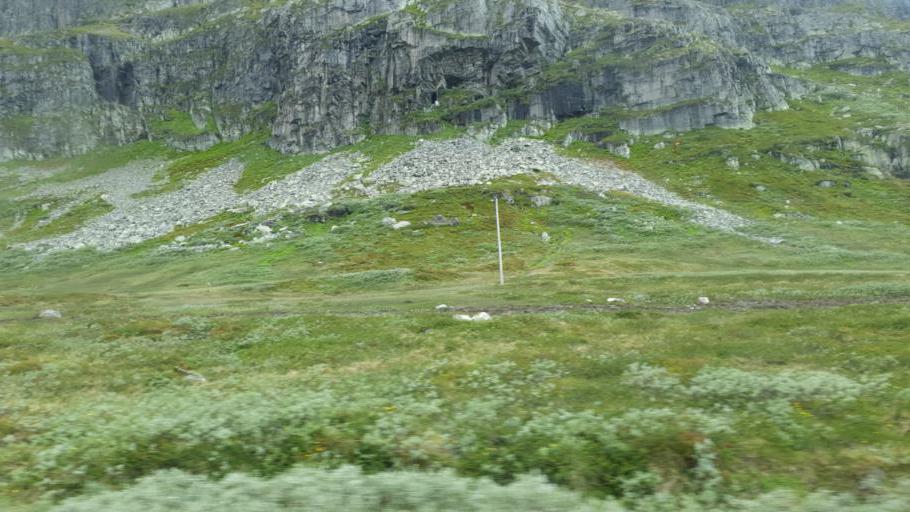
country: NO
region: Oppland
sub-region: Vestre Slidre
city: Slidre
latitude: 61.3050
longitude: 8.8077
